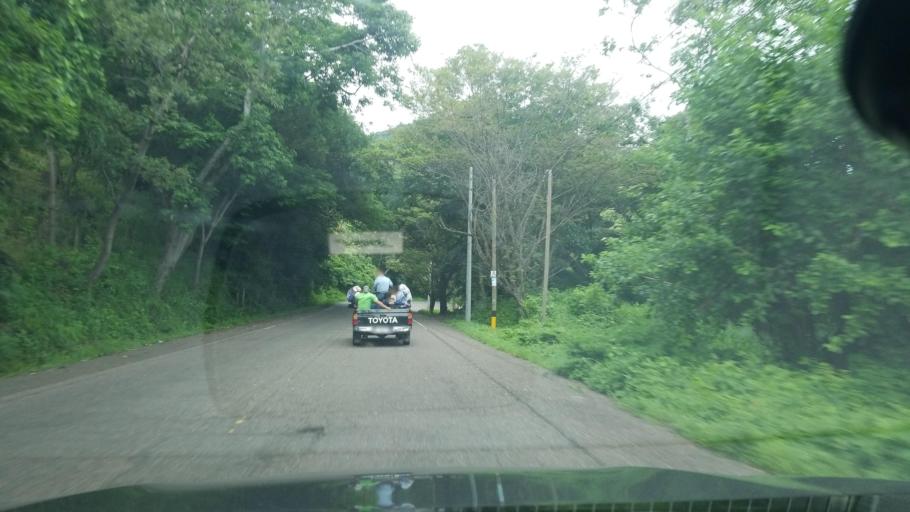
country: HN
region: Choluteca
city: Corpus
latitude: 13.3708
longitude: -87.0389
